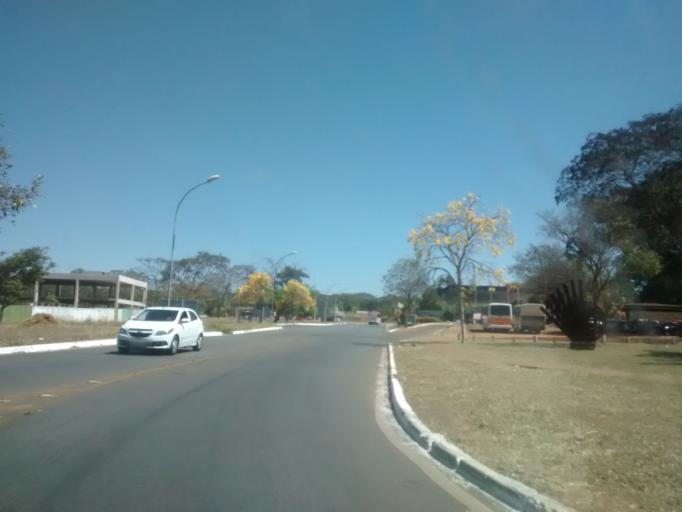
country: BR
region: Federal District
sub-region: Brasilia
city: Brasilia
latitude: -15.7606
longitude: -47.8730
